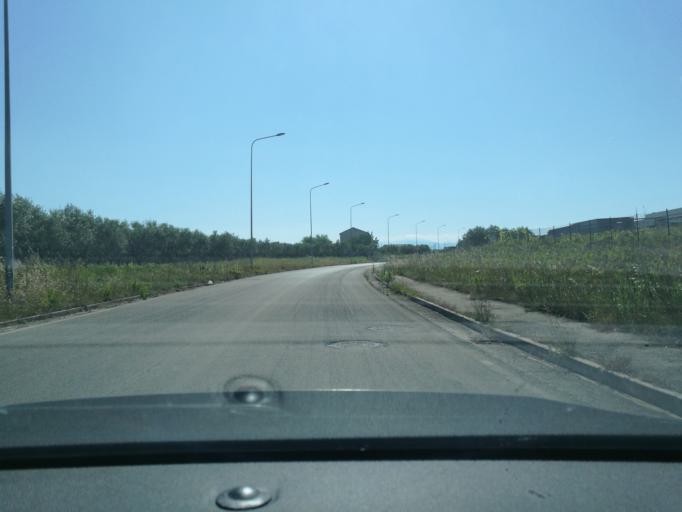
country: IT
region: Abruzzo
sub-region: Provincia di Chieti
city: Vasto
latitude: 42.1648
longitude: 14.6880
